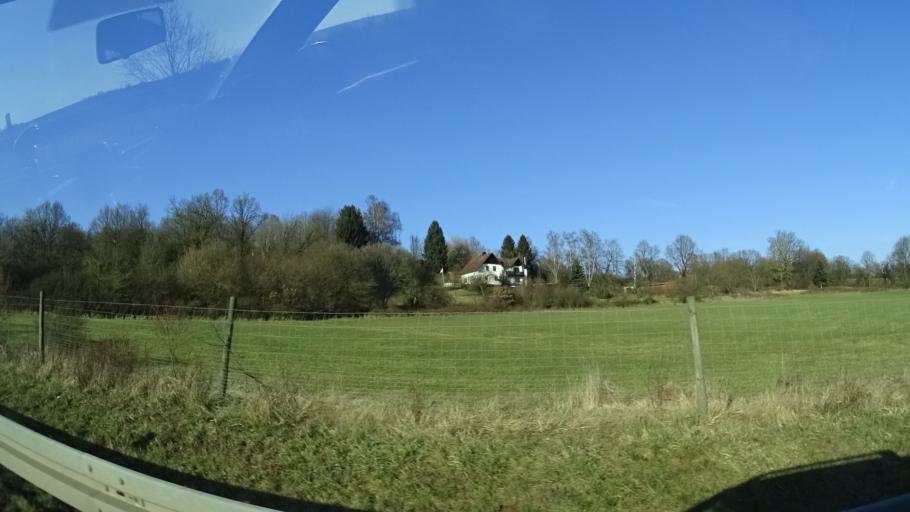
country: DE
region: Hesse
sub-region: Regierungsbezirk Darmstadt
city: Steinau an der Strasse
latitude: 50.3263
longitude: 9.4850
